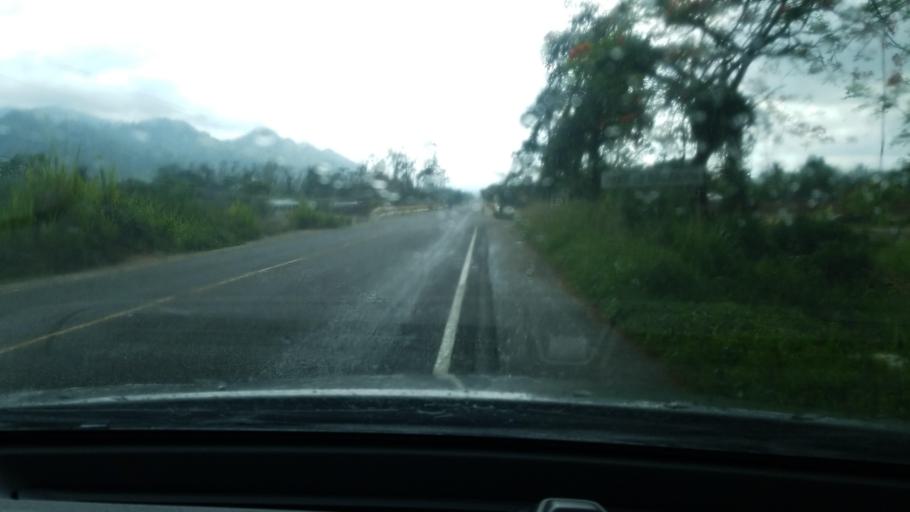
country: HN
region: Cortes
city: Rio Chiquito
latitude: 15.6305
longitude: -88.2498
